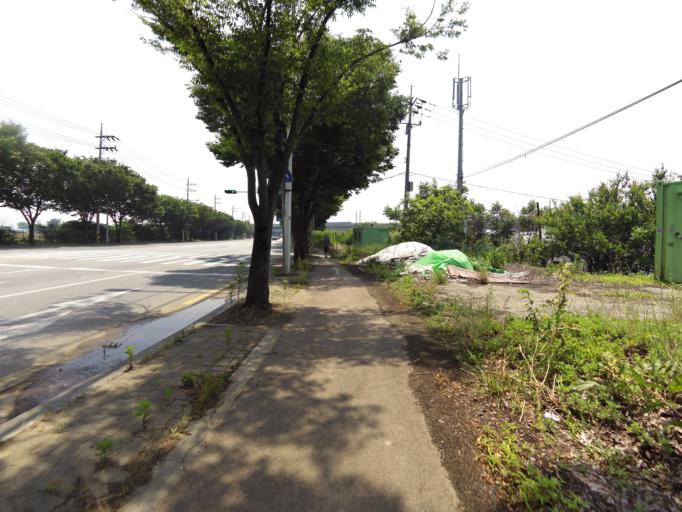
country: KR
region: Gyeongsangbuk-do
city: Gyeongsan-si
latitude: 35.8555
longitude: 128.7221
